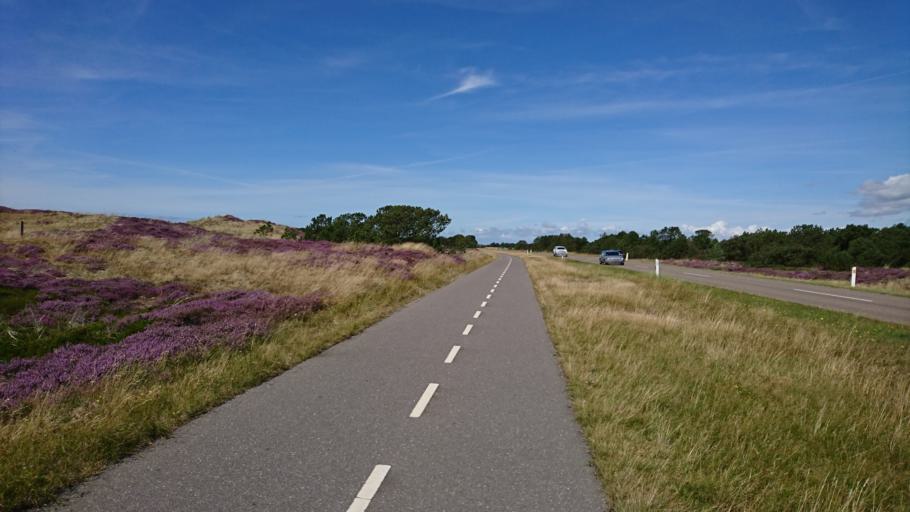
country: DK
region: South Denmark
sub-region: Fano Kommune
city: Nordby
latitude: 55.4109
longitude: 8.4106
